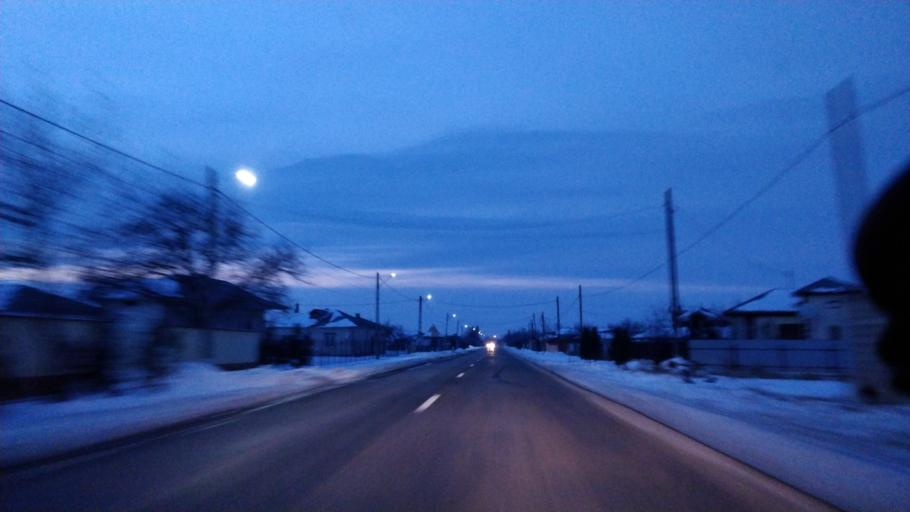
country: RO
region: Vrancea
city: Vulturu de Sus
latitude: 45.6111
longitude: 27.4396
